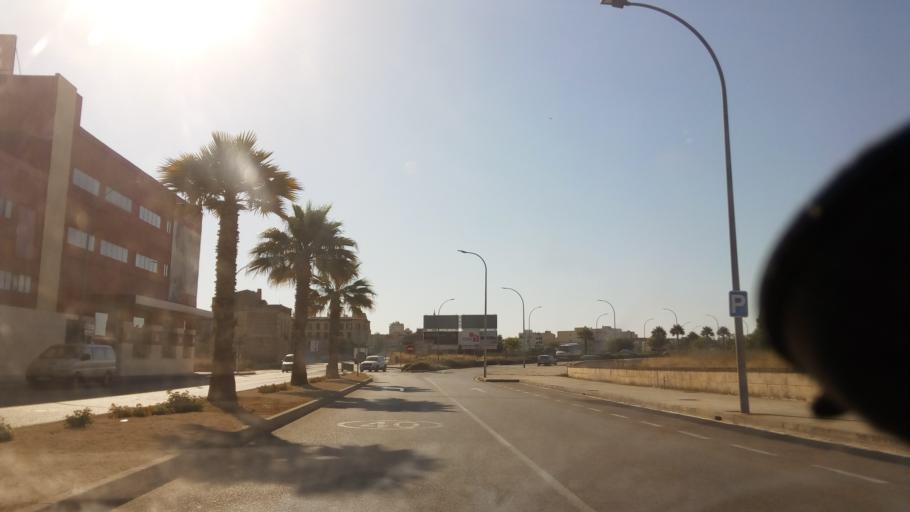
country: ES
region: Balearic Islands
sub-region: Illes Balears
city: Manacor
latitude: 39.5721
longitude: 3.1955
